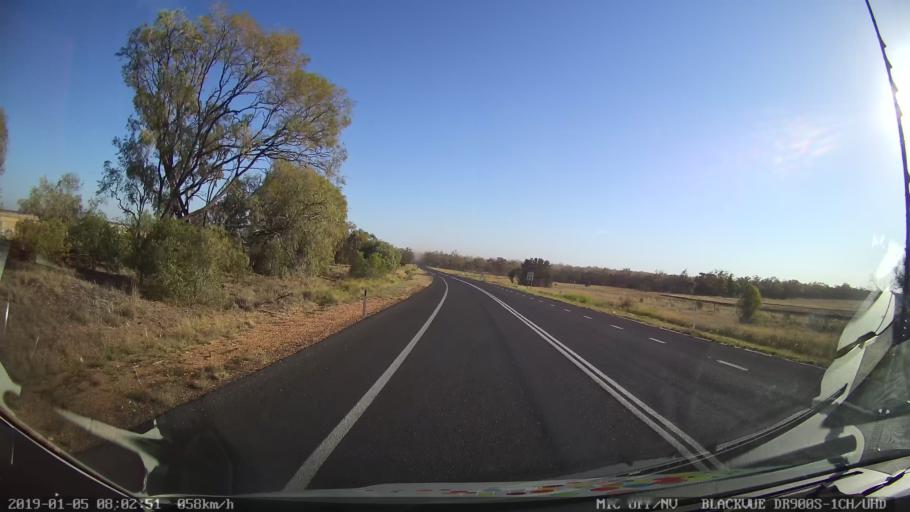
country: AU
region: New South Wales
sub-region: Gilgandra
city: Gilgandra
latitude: -31.6720
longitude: 148.7150
